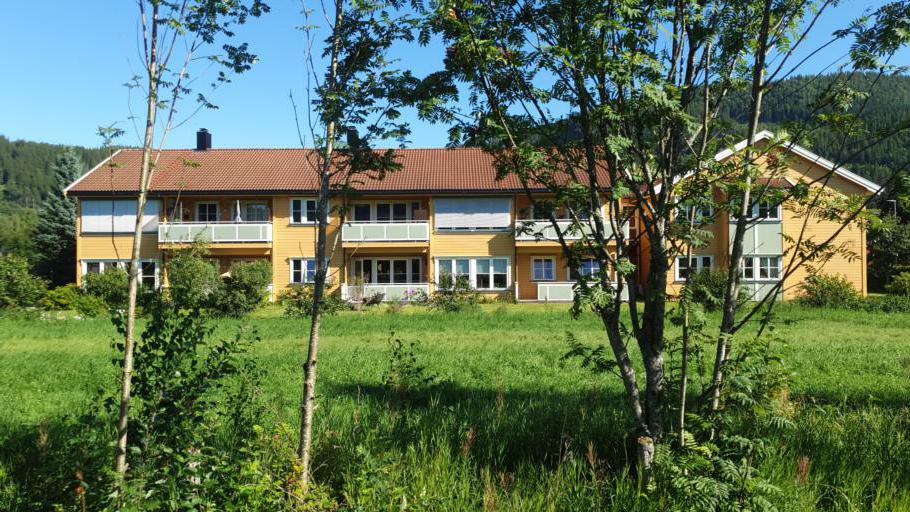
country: NO
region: Sor-Trondelag
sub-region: Orkdal
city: Orkanger
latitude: 63.2858
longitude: 9.8413
